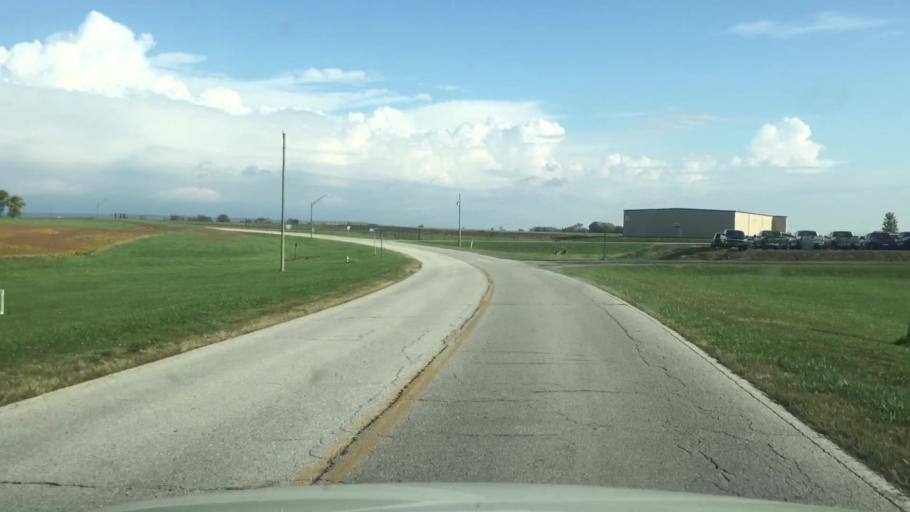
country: US
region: Missouri
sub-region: Boone County
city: Ashland
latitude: 38.8201
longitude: -92.2218
